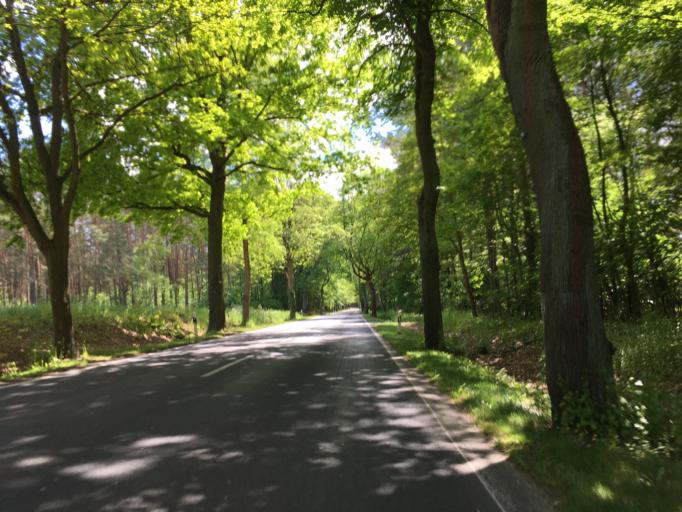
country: DE
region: Brandenburg
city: Marienwerder
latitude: 52.7841
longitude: 13.5562
